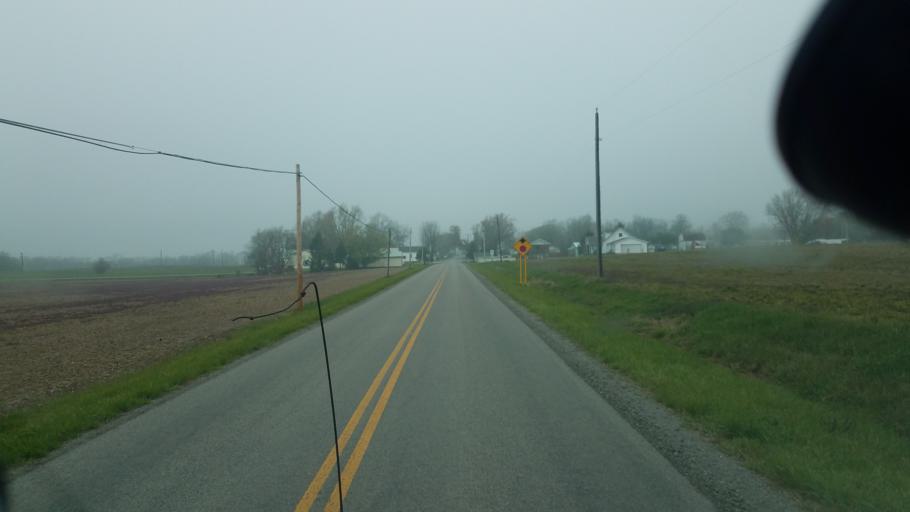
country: US
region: Ohio
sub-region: Logan County
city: De Graff
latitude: 40.3434
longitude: -83.9283
